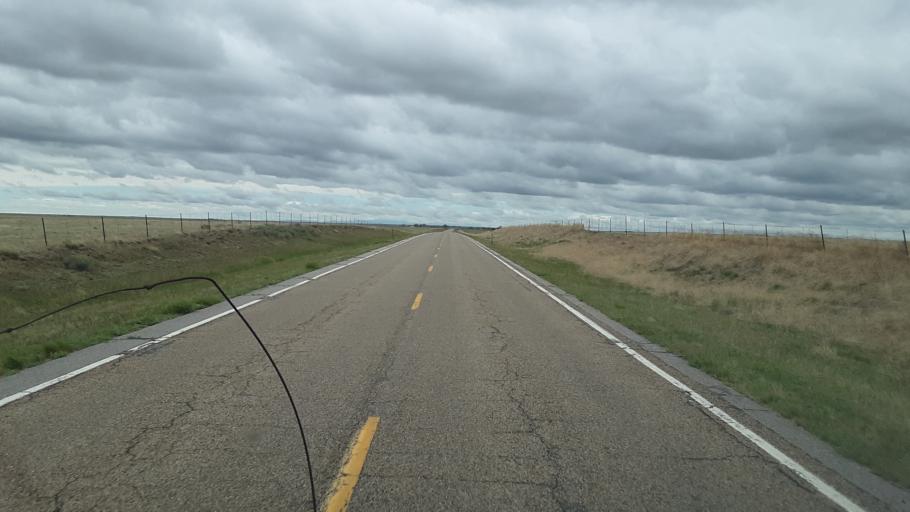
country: US
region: Colorado
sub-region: El Paso County
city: Ellicott
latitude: 38.8394
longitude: -103.9175
